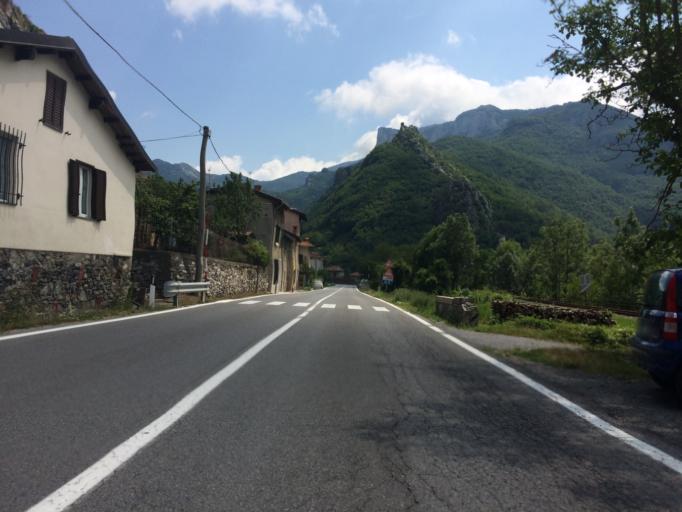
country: IT
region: Piedmont
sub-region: Provincia di Cuneo
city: Ormea
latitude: 44.1582
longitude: 7.9527
